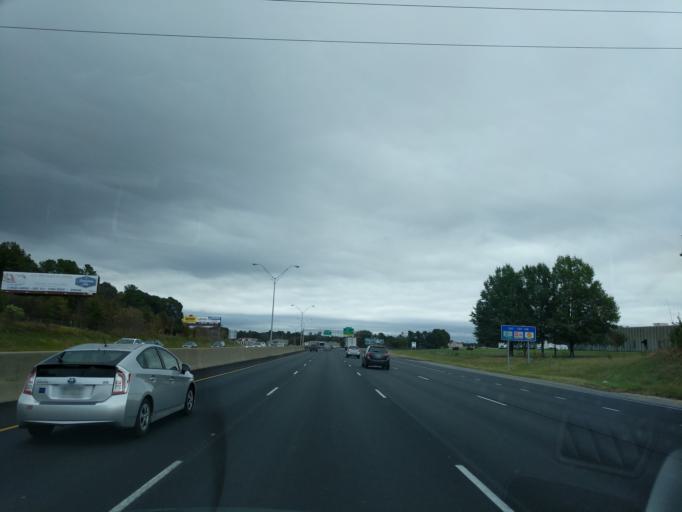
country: US
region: North Carolina
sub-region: Alamance County
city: Graham
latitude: 36.0612
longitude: -79.3908
